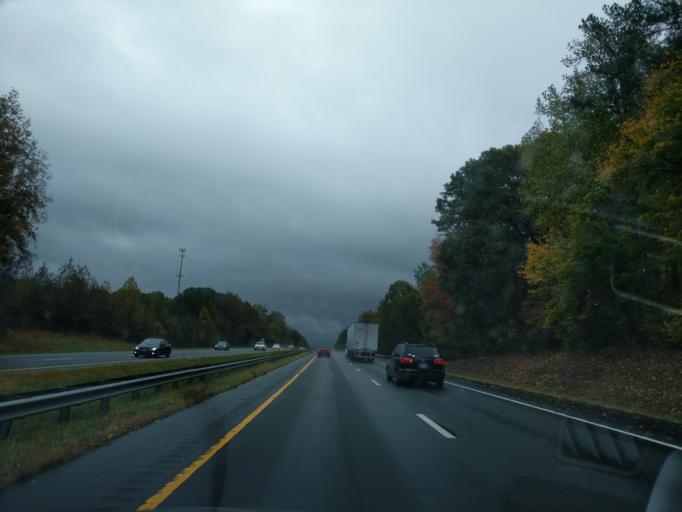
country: US
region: North Carolina
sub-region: Orange County
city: Hillsborough
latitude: 36.0390
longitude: -79.0227
